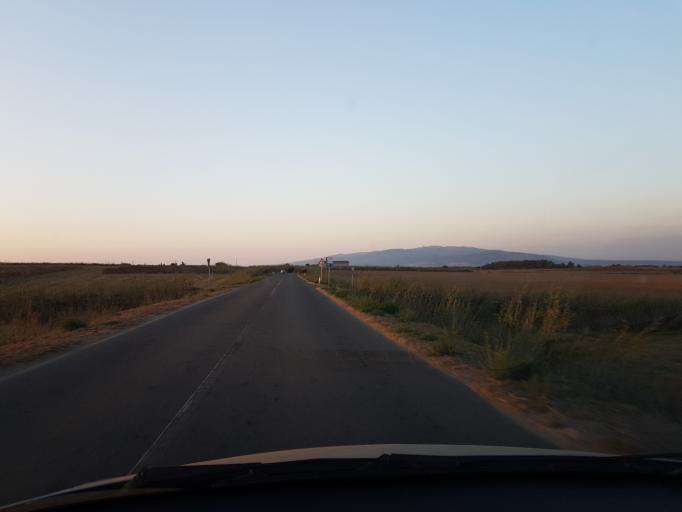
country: IT
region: Sardinia
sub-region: Provincia di Oristano
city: Nurachi
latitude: 39.9758
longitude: 8.4533
